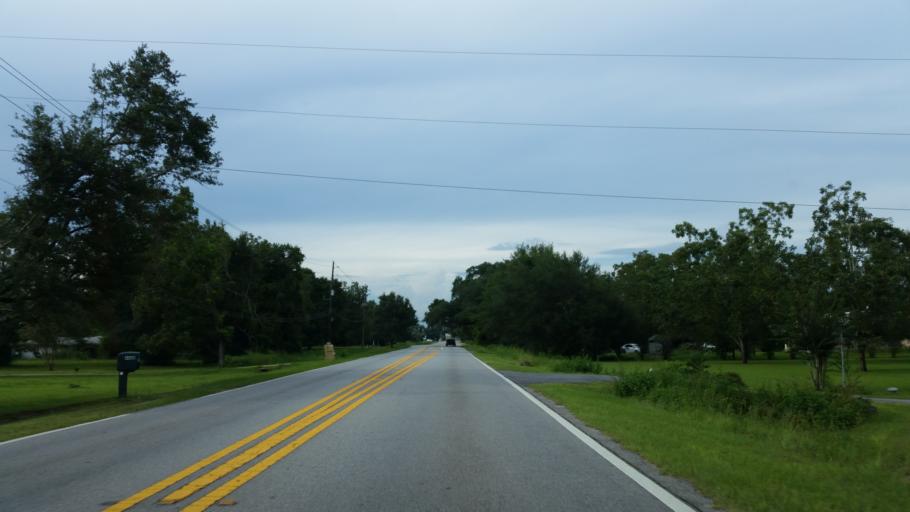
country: US
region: Florida
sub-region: Santa Rosa County
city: Pace
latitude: 30.5979
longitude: -87.1113
